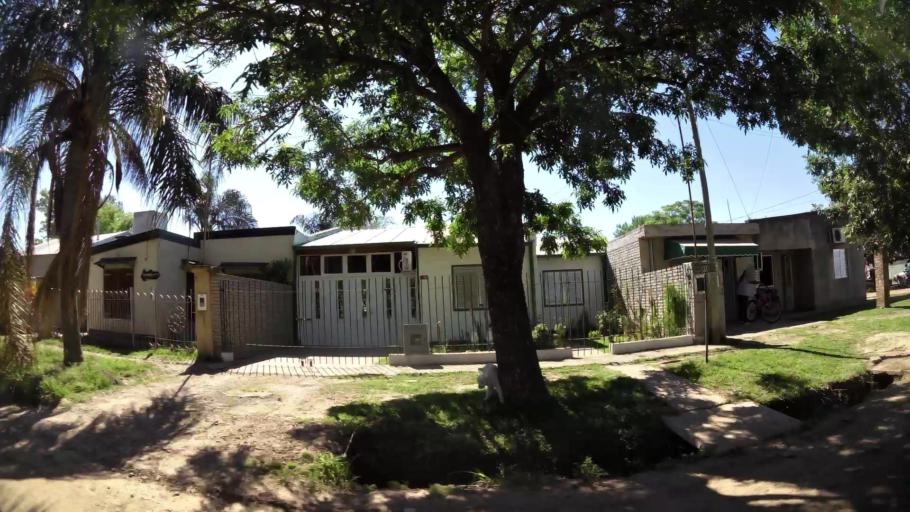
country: AR
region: Santa Fe
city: Esperanza
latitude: -31.4635
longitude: -60.9327
